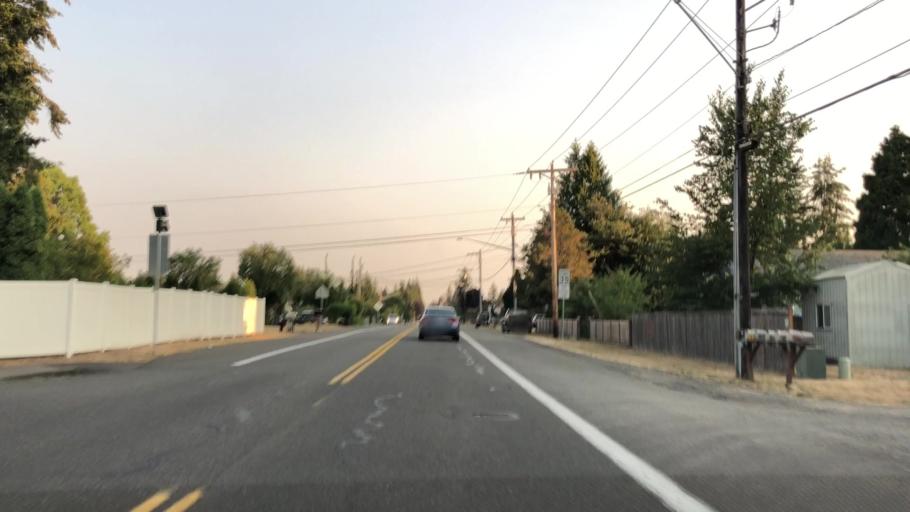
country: US
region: Washington
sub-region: Snohomish County
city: Marysville
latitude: 48.0834
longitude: -122.1622
